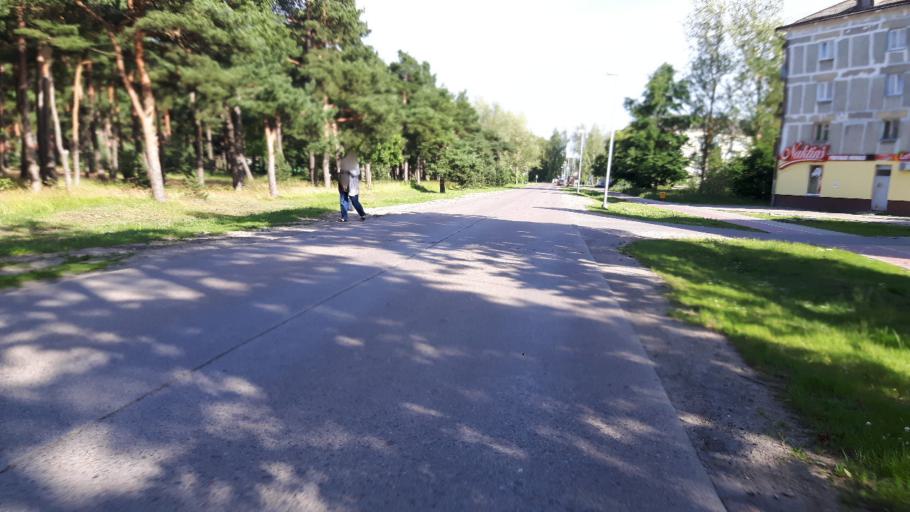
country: LV
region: Liepaja
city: Vec-Liepaja
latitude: 56.5469
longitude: 21.0166
